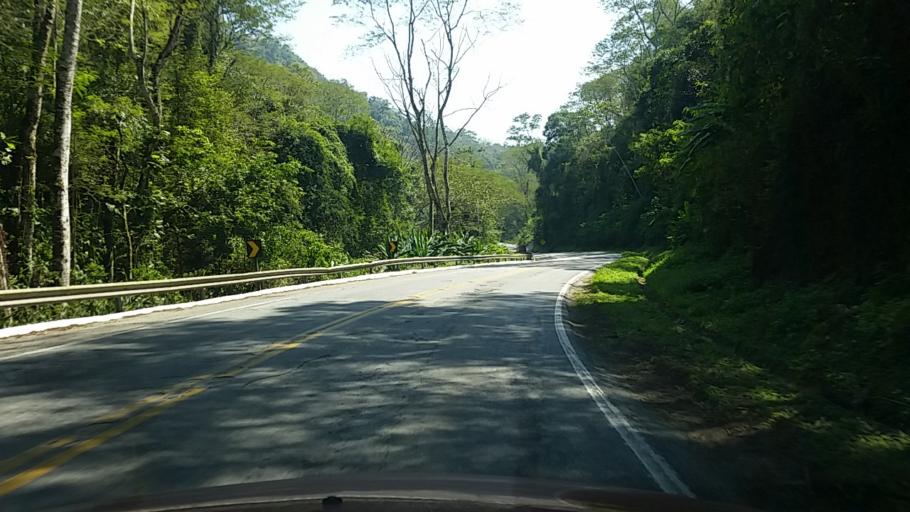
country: BR
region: Sao Paulo
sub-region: Miracatu
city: Miracatu
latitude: -24.3335
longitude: -47.5042
